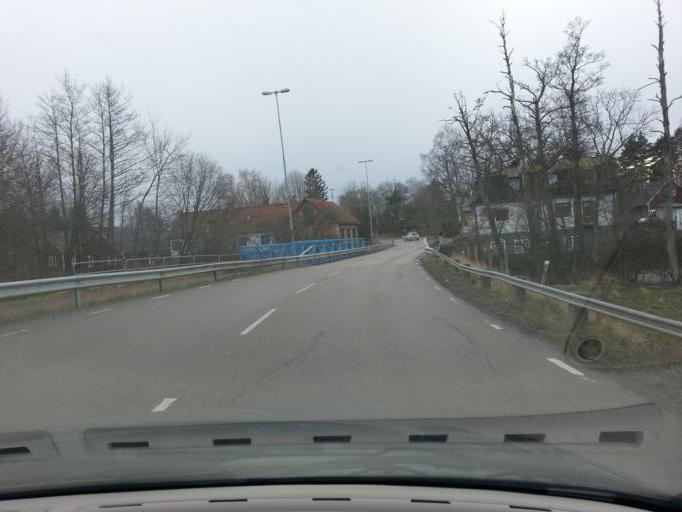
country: SE
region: Skane
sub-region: Klippans Kommun
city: Ljungbyhed
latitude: 56.0807
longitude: 13.2381
